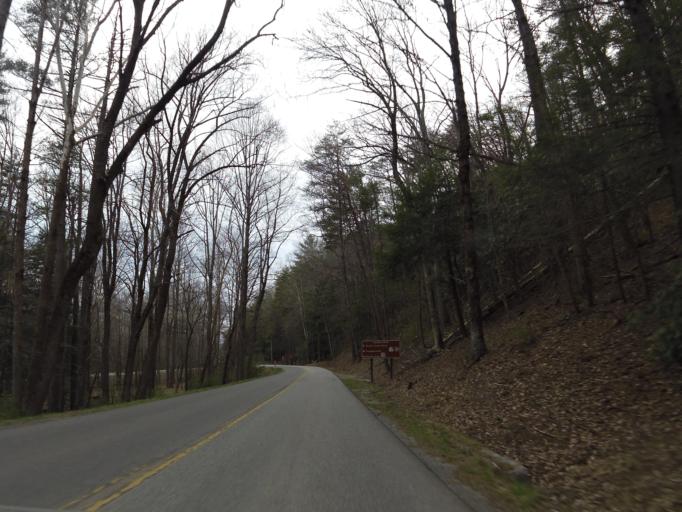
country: US
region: Tennessee
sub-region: Blount County
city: Wildwood
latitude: 35.6063
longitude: -83.7724
